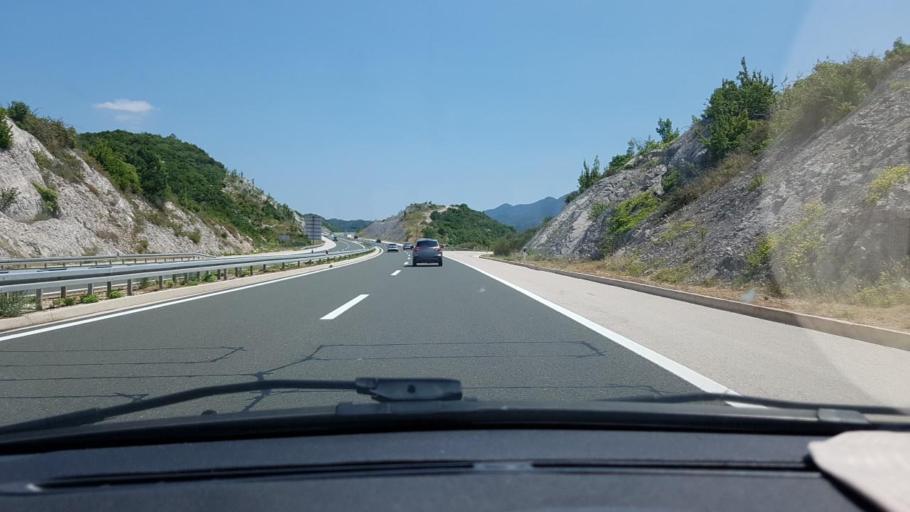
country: HR
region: Splitsko-Dalmatinska
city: Vrgorac
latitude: 43.2122
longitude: 17.2707
